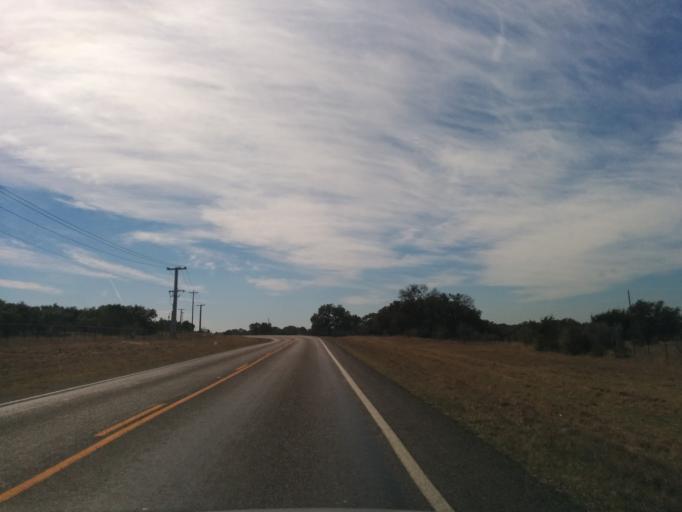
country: US
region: Texas
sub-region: Bexar County
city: Fair Oaks Ranch
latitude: 29.8795
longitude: -98.5584
